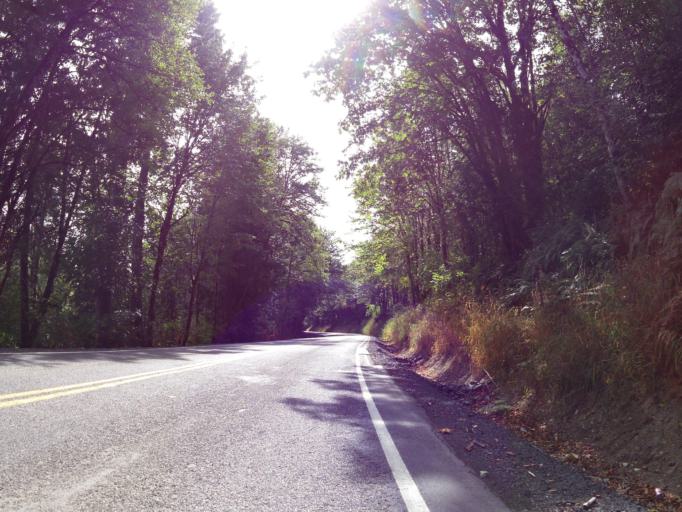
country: US
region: Washington
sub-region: Lewis County
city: Napavine
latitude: 46.5567
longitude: -122.9587
